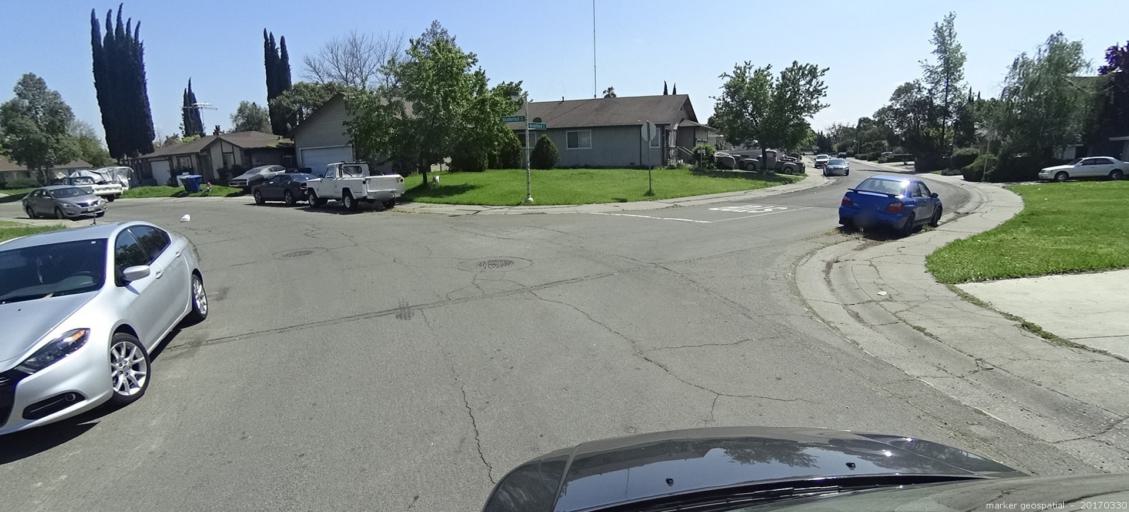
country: US
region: California
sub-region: Sacramento County
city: Florin
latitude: 38.4636
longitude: -121.4300
